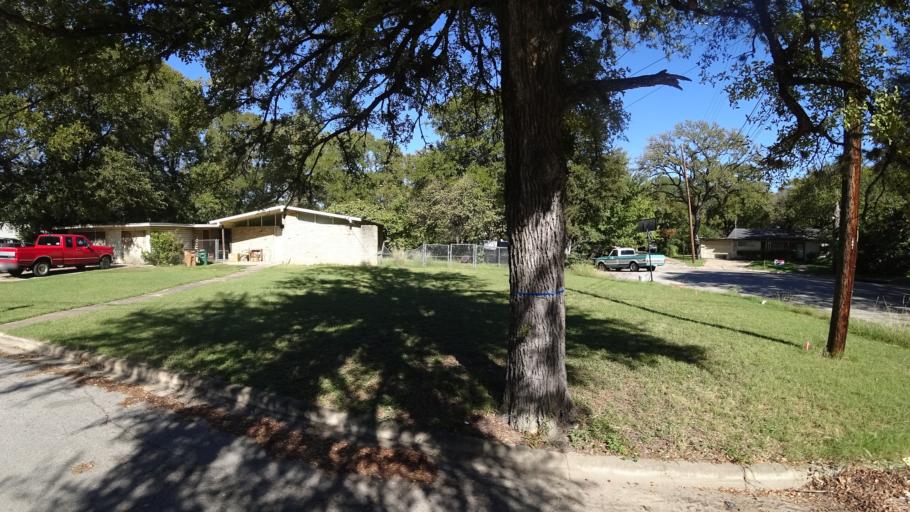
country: US
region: Texas
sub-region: Travis County
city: Austin
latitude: 30.2837
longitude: -97.6894
